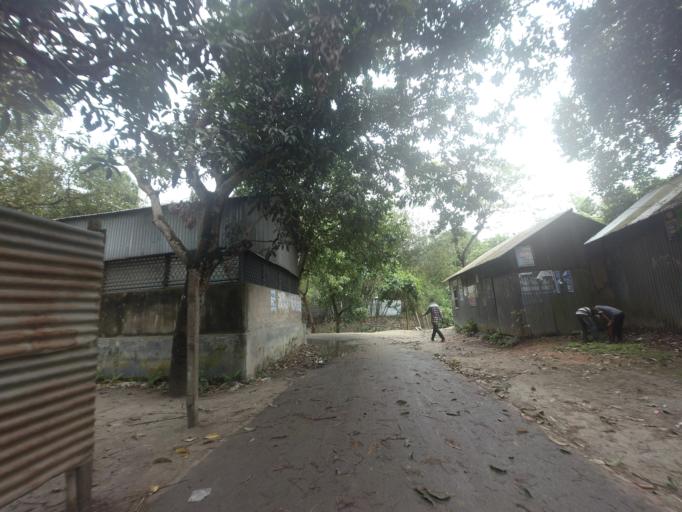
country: BD
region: Rajshahi
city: Sirajganj
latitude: 24.3271
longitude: 89.6950
